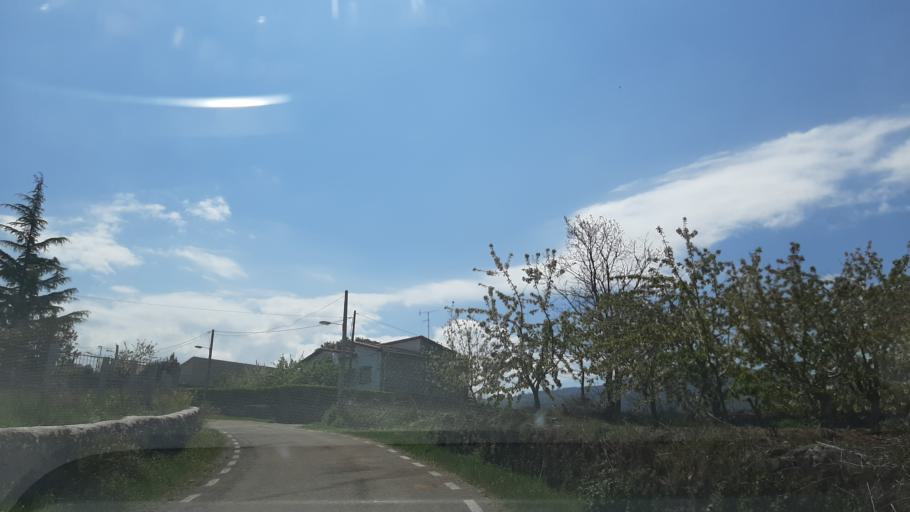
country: ES
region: Castille and Leon
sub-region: Provincia de Salamanca
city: Navarredonda de la Rinconada
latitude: 40.6146
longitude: -6.0195
